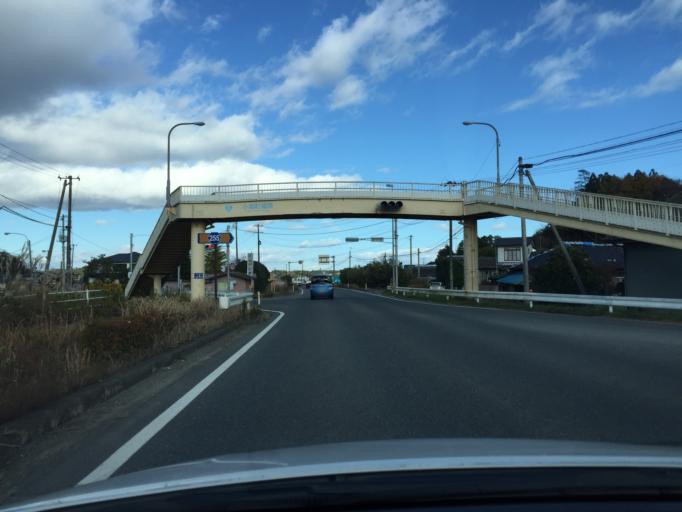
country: JP
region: Fukushima
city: Namie
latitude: 37.5510
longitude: 141.0062
